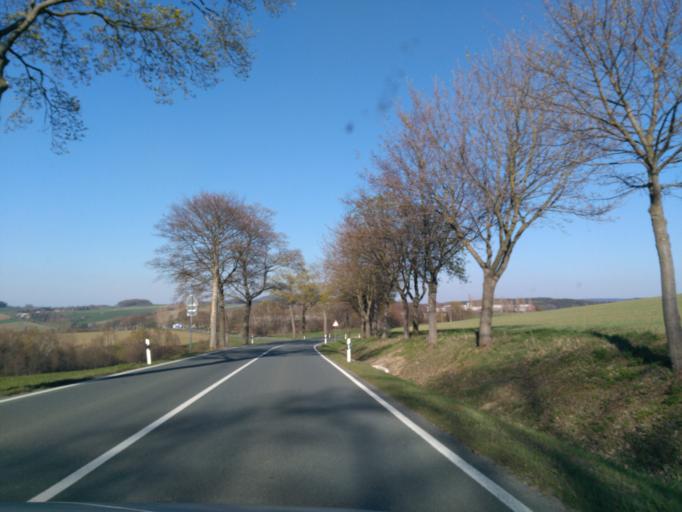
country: DE
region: Saxony
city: Schlettau
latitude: 50.5486
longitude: 12.9366
